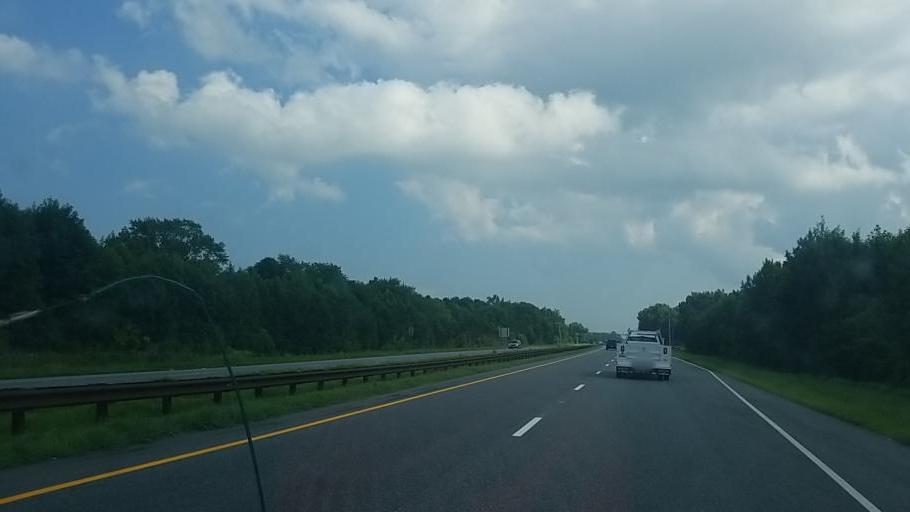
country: US
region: Delaware
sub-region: Sussex County
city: Selbyville
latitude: 38.4391
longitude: -75.2254
